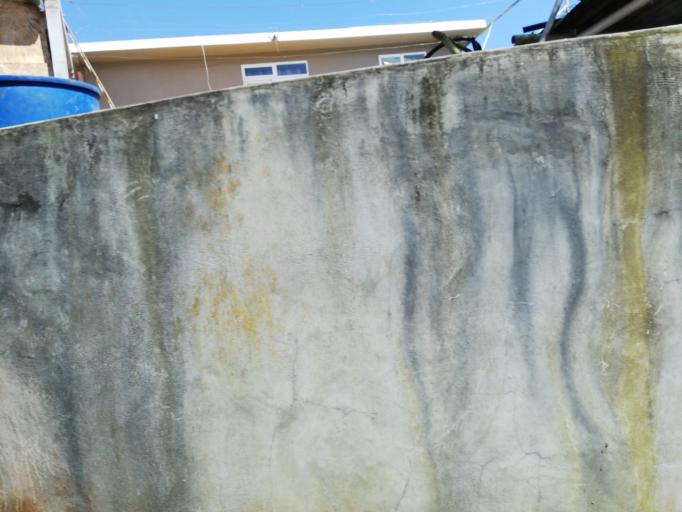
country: MU
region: Moka
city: Moka
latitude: -20.2240
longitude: 57.5077
